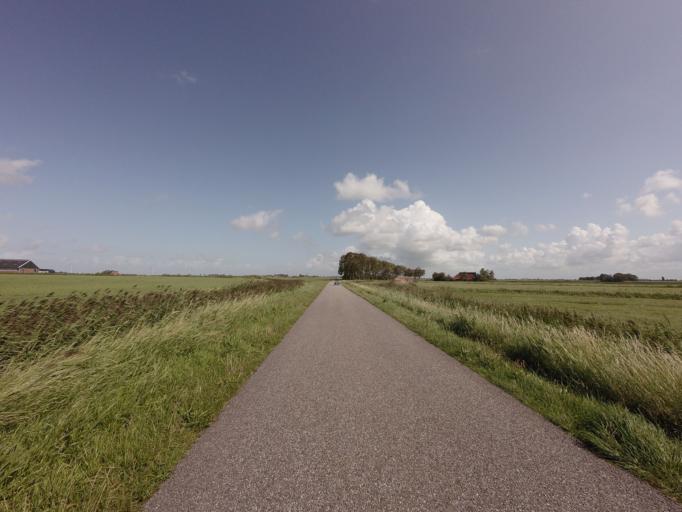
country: NL
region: Friesland
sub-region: Sudwest Fryslan
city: Makkum
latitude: 53.0633
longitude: 5.4364
